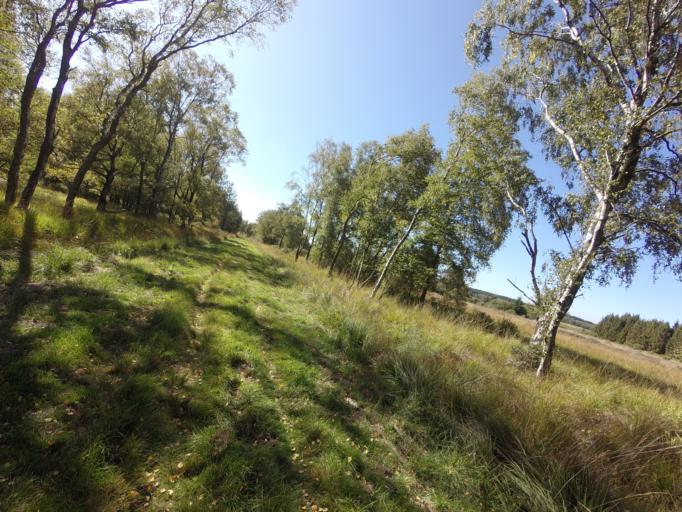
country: DE
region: North Rhine-Westphalia
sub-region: Regierungsbezirk Koln
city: Roetgen
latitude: 50.6034
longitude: 6.1598
